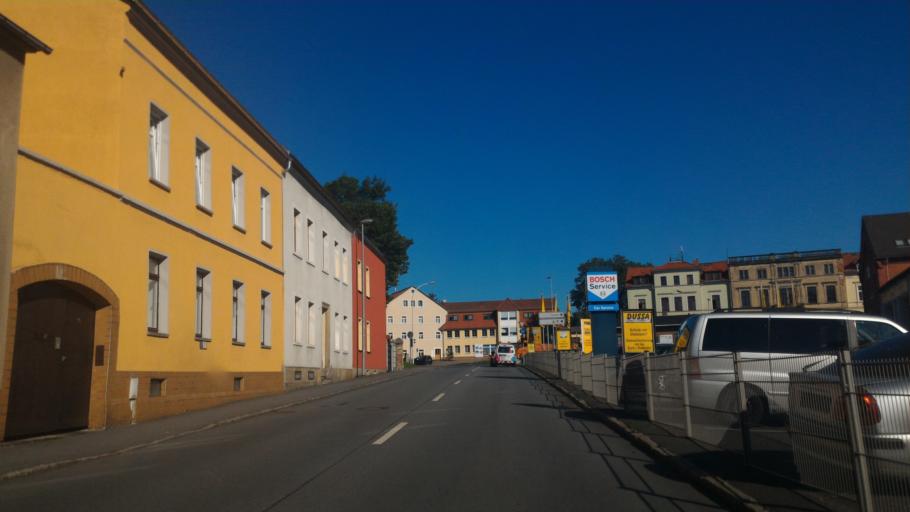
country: DE
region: Saxony
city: Zittau
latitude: 50.8972
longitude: 14.8179
